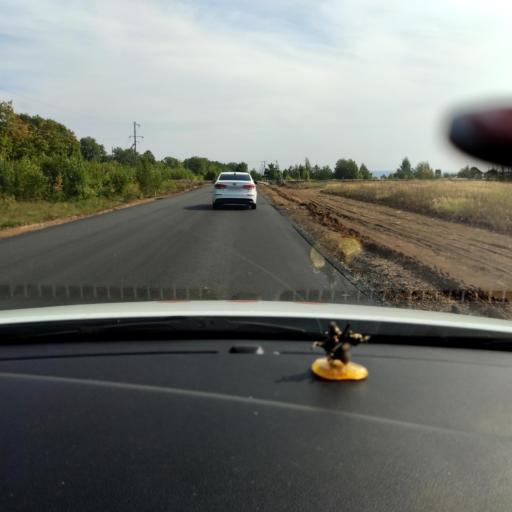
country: RU
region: Tatarstan
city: Verkhniy Uslon
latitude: 55.7363
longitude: 48.9535
